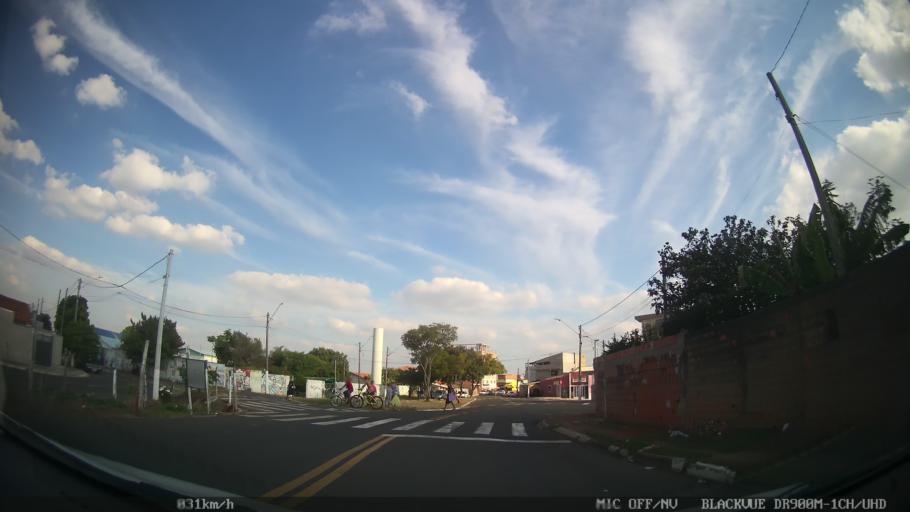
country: BR
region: Sao Paulo
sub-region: Hortolandia
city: Hortolandia
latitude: -22.8516
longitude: -47.1972
